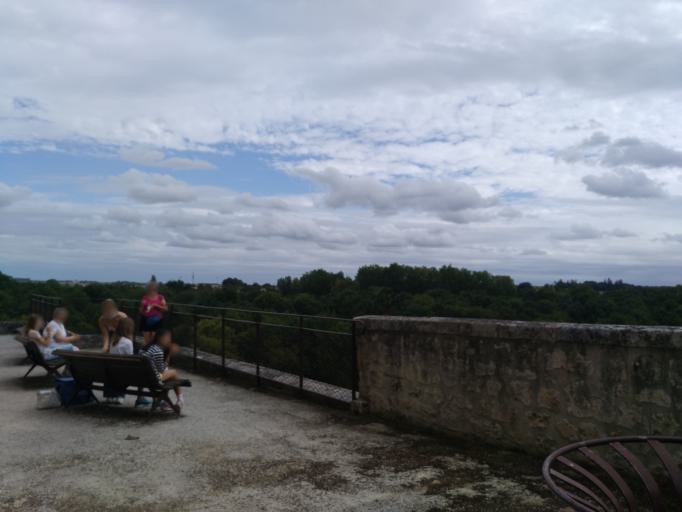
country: FR
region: Poitou-Charentes
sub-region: Departement de la Charente-Maritime
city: Pons
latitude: 45.5778
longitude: -0.5477
